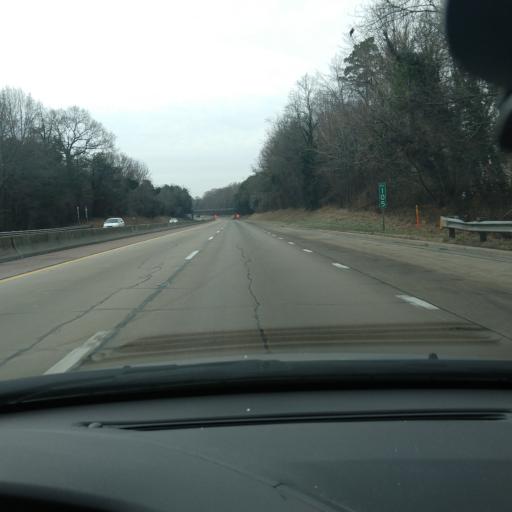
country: US
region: North Carolina
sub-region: Forsyth County
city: Winston-Salem
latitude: 36.0446
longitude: -80.2382
